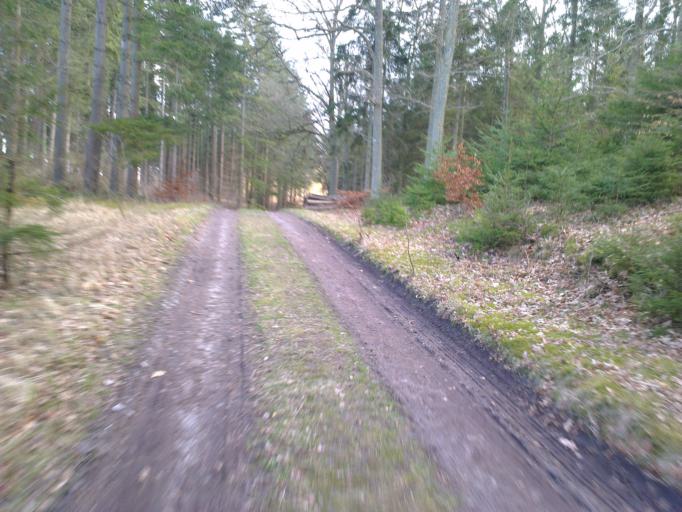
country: DK
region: Capital Region
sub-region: Frederikssund Kommune
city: Jaegerspris
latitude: 55.9158
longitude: 11.9615
